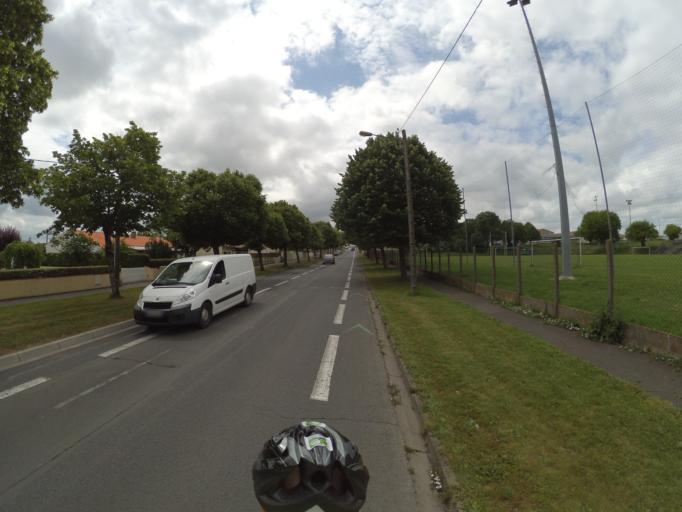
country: FR
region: Poitou-Charentes
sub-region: Departement de la Charente-Maritime
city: Rochefort
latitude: 45.9548
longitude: -0.9690
